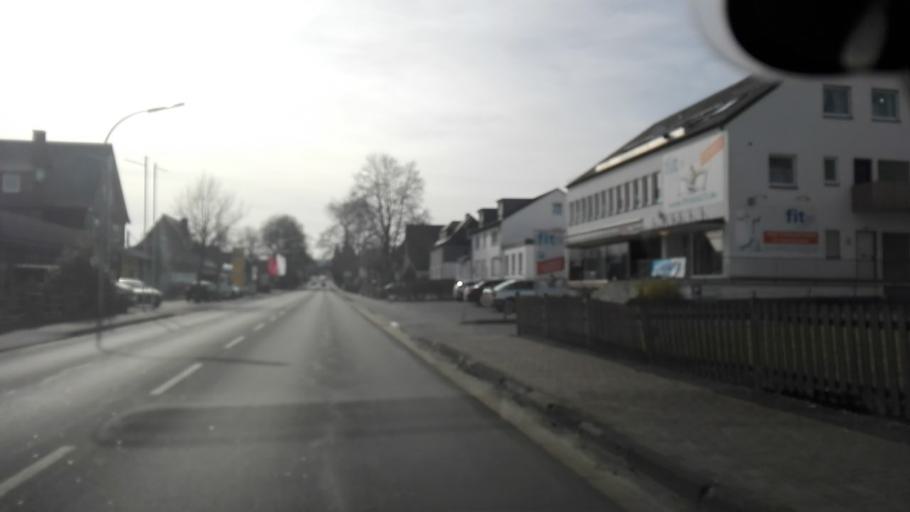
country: DE
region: North Rhine-Westphalia
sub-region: Regierungsbezirk Arnsberg
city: Schmallenberg
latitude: 51.1577
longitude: 8.2907
